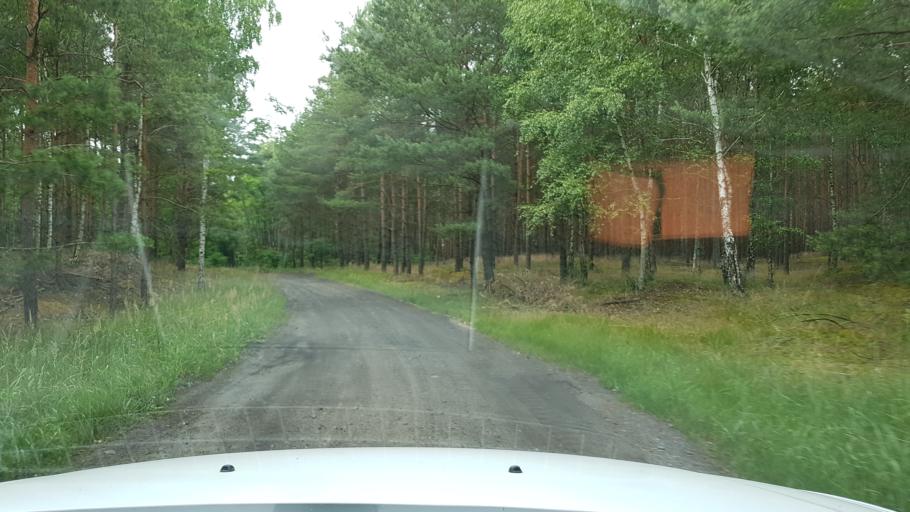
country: PL
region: West Pomeranian Voivodeship
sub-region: Powiat mysliborski
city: Boleszkowice
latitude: 52.6399
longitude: 14.5501
